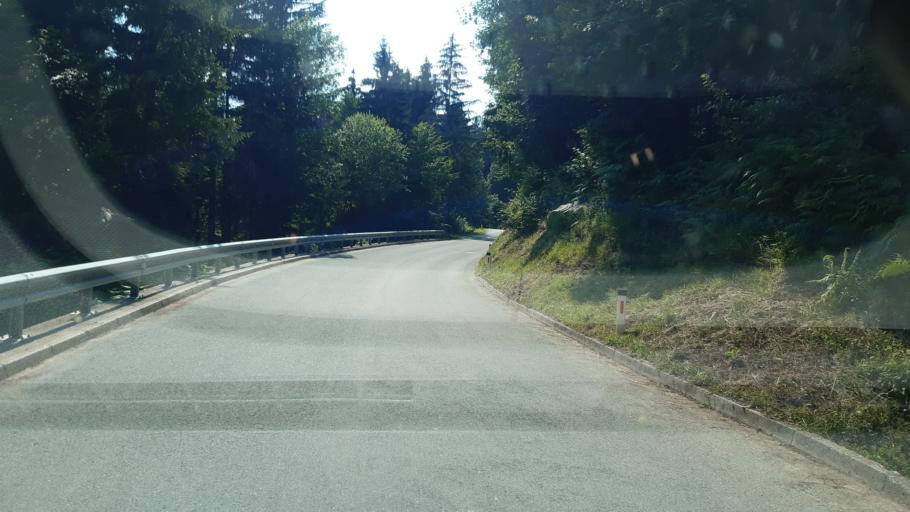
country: SI
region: Trzic
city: Bistrica pri Trzicu
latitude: 46.3595
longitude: 14.2559
